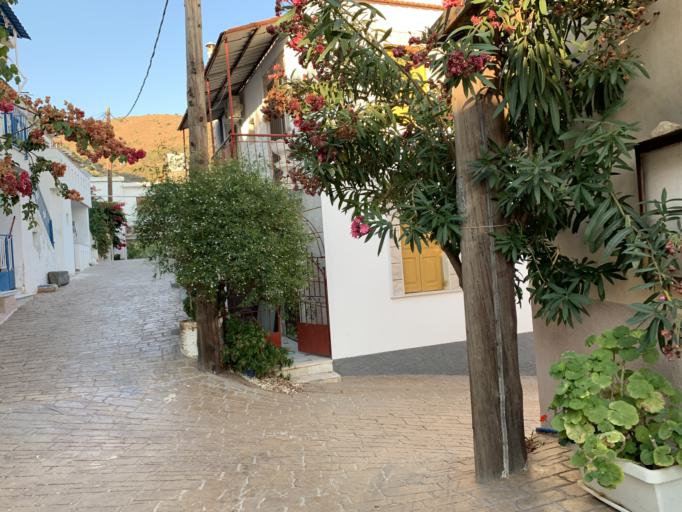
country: GR
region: North Aegean
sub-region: Chios
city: Vrontados
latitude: 38.5271
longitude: 25.8678
